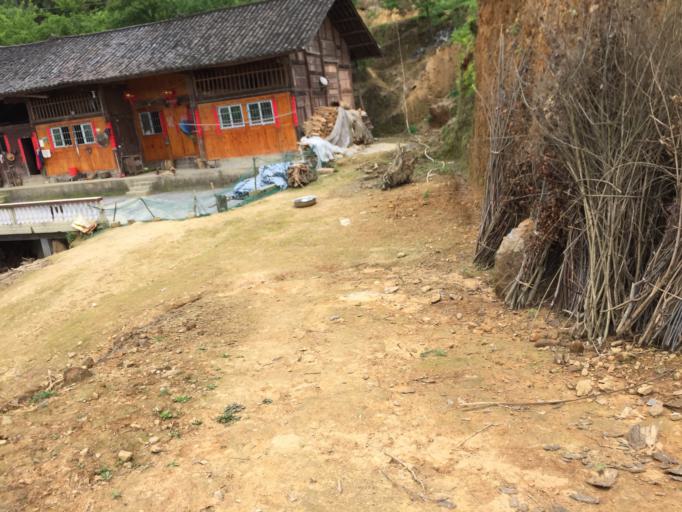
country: CN
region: Guizhou Sheng
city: Xujiaba
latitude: 27.6780
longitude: 108.0856
